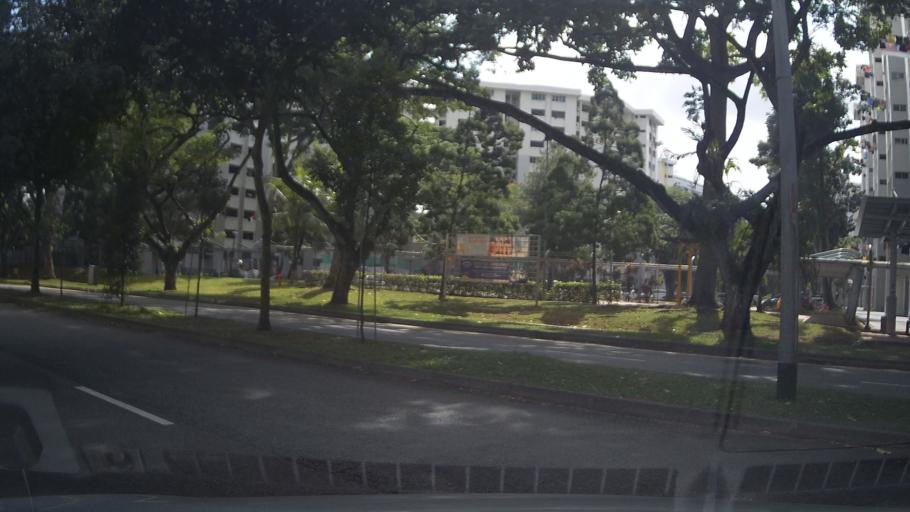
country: SG
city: Singapore
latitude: 1.3203
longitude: 103.7671
